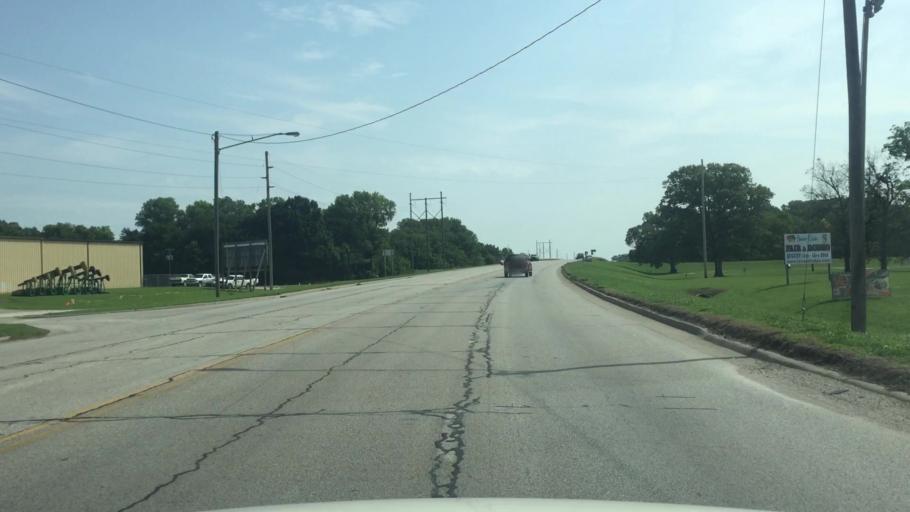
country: US
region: Kansas
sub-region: Montgomery County
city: Coffeyville
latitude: 37.0406
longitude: -95.5953
